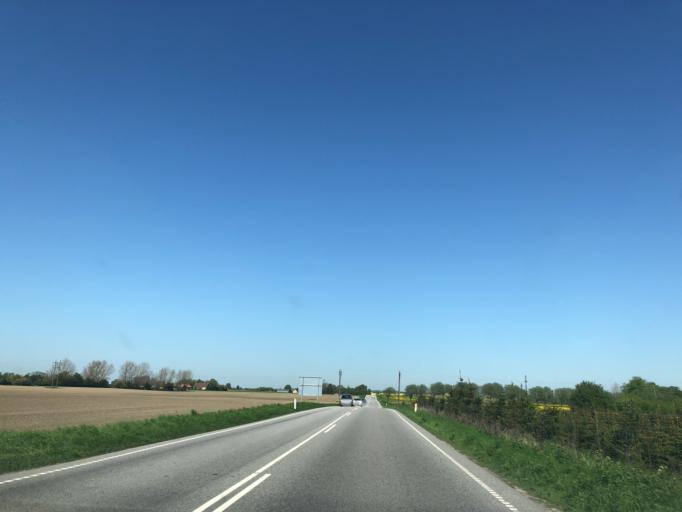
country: DK
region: Zealand
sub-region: Slagelse Kommune
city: Skaelskor
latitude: 55.3029
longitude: 11.2882
